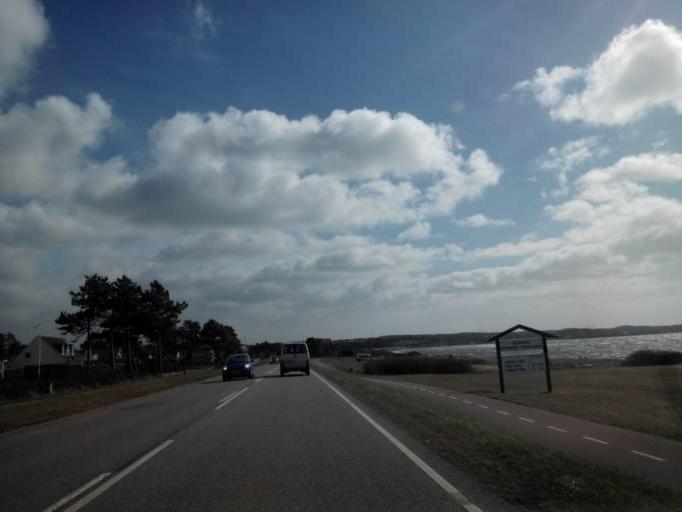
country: DK
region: Central Jutland
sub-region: Syddjurs Kommune
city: Ebeltoft
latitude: 56.2216
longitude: 10.6666
